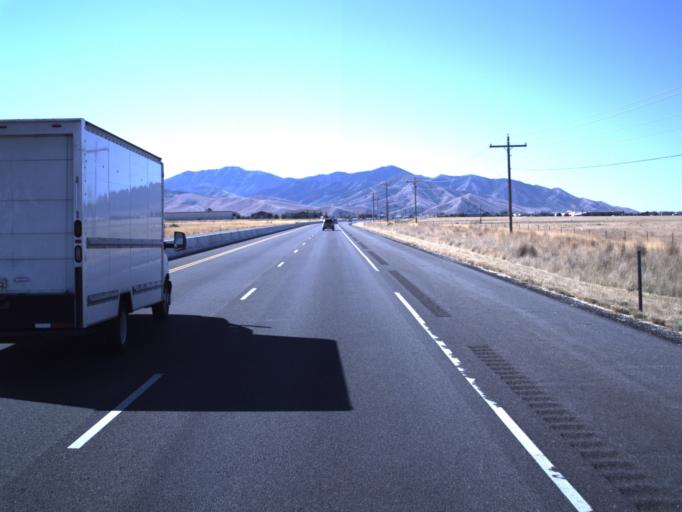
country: US
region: Utah
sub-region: Tooele County
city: Erda
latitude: 40.5843
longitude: -112.2940
